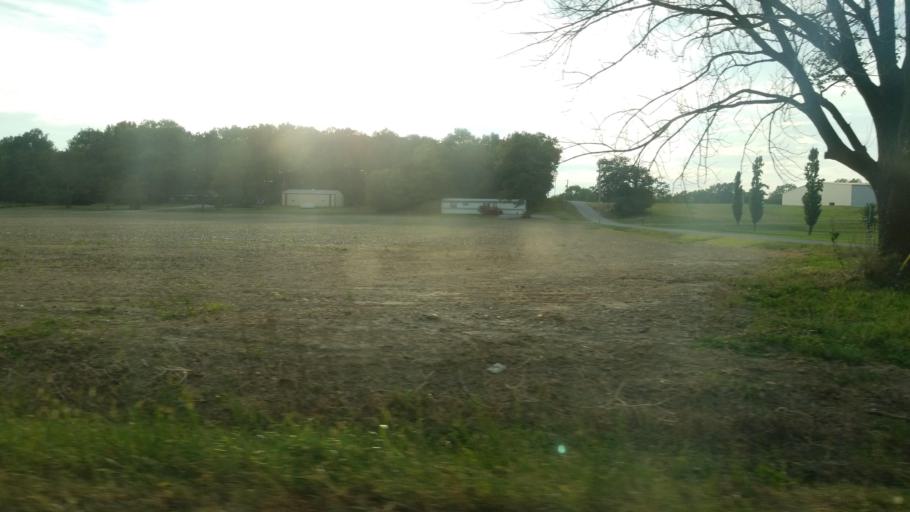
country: US
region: Illinois
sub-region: Saline County
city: Harrisburg
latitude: 37.7937
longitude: -88.5401
